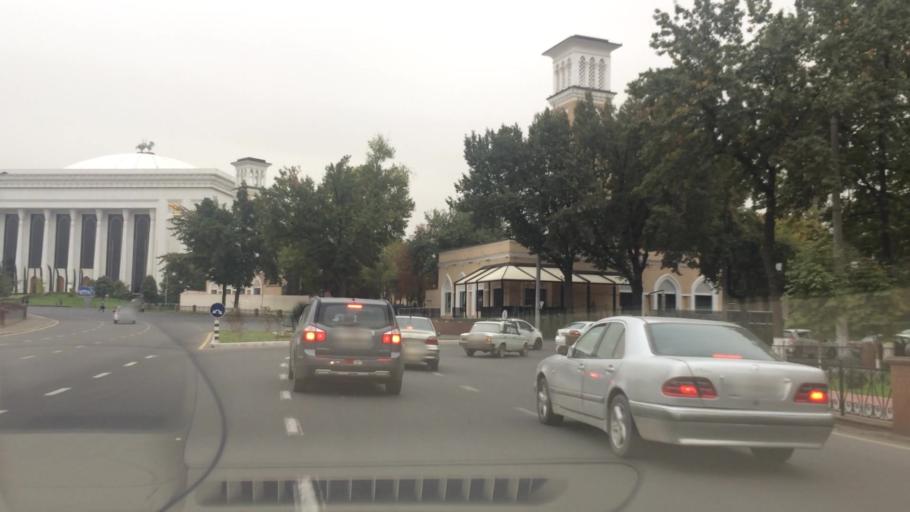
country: UZ
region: Toshkent Shahri
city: Tashkent
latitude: 41.3101
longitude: 69.2790
